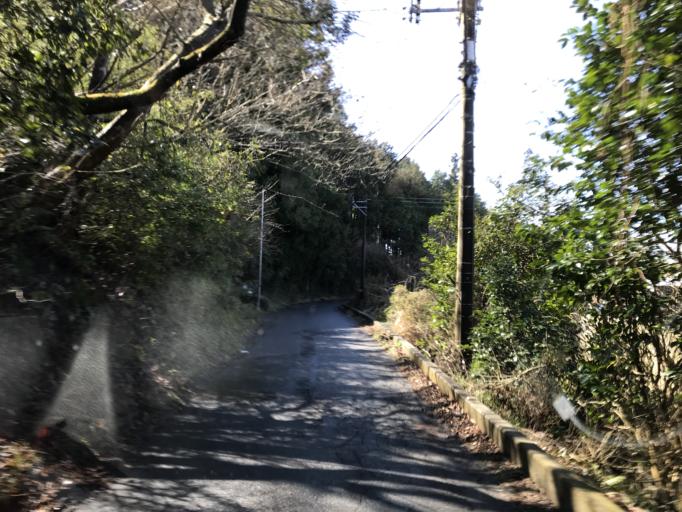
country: JP
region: Shizuoka
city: Fujinomiya
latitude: 35.2463
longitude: 138.6615
